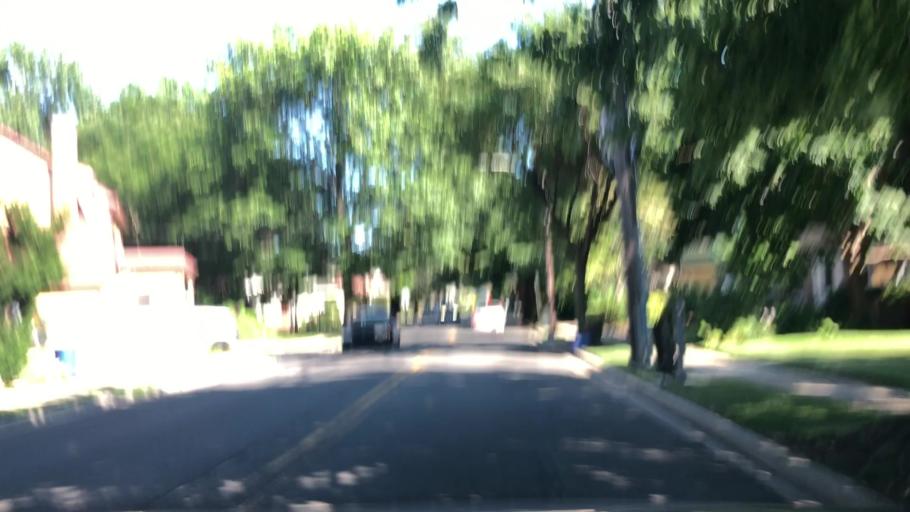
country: US
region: New York
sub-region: Nassau County
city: Floral Park
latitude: 40.7222
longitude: -73.7061
